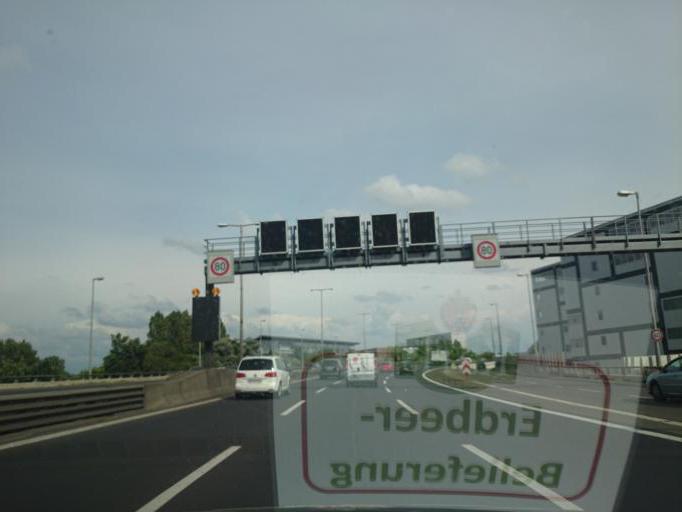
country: DE
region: Berlin
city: Tempelhof Bezirk
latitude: 52.4653
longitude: 13.4004
